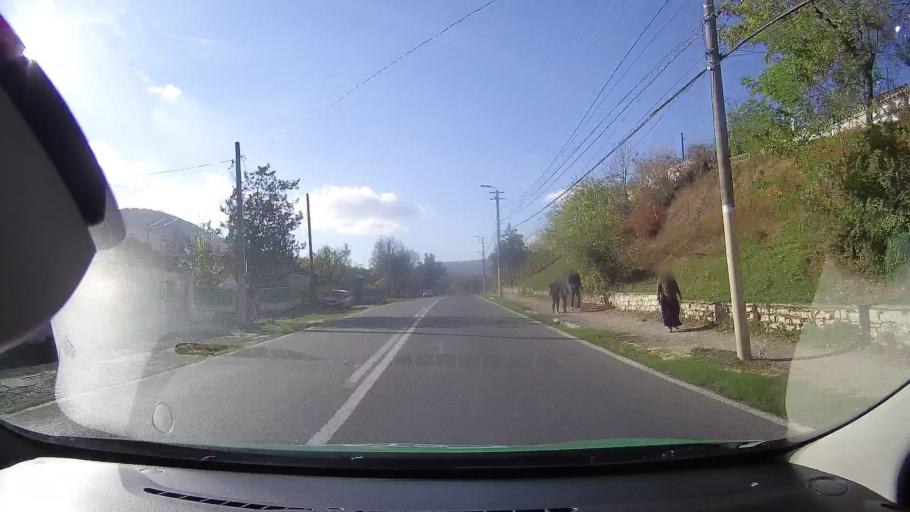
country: RO
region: Tulcea
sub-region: Oras Babadag
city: Babadag
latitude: 44.8856
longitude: 28.7028
